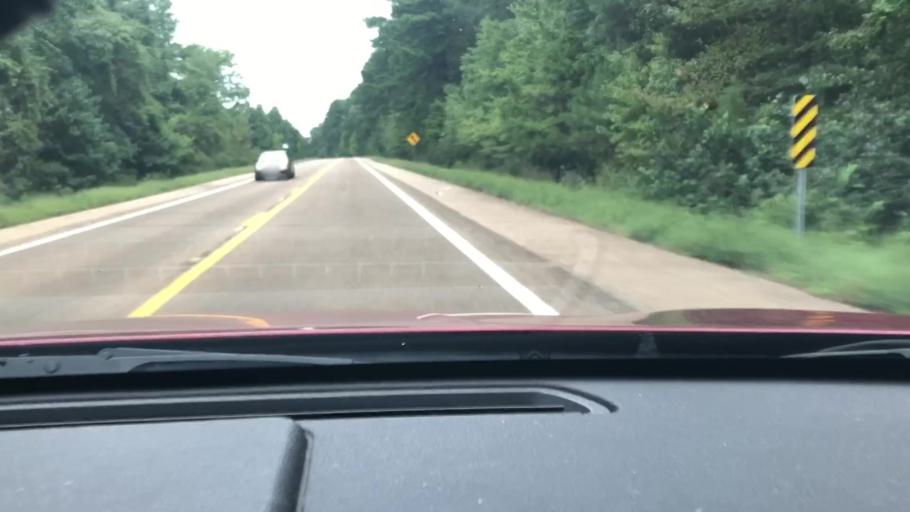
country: US
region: Arkansas
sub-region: Miller County
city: Texarkana
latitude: 33.4193
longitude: -93.8332
